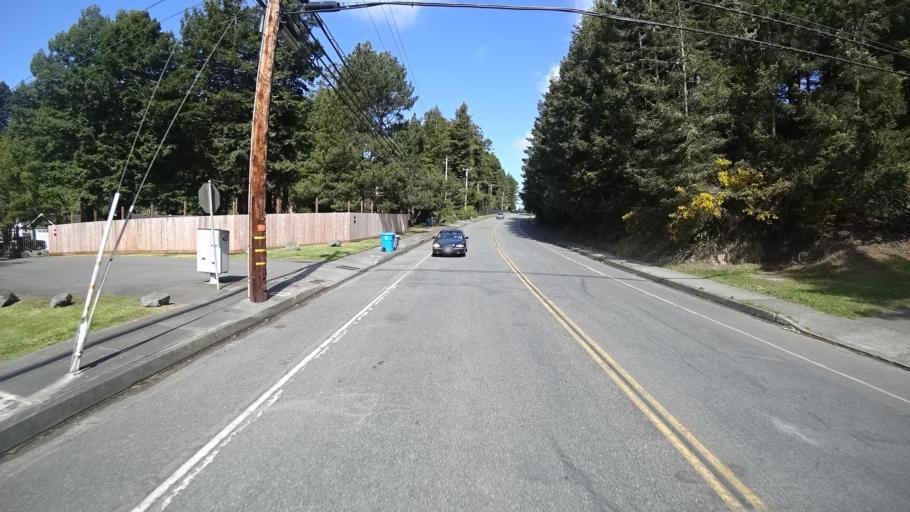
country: US
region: California
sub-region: Humboldt County
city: Cutten
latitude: 40.7682
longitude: -124.1583
